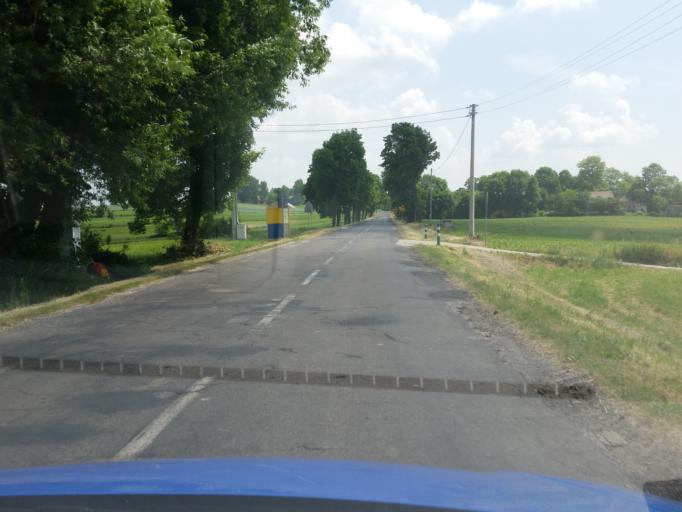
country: PL
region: Swietokrzyskie
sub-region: Powiat pinczowski
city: Dzialoszyce
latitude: 50.3245
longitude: 20.2705
